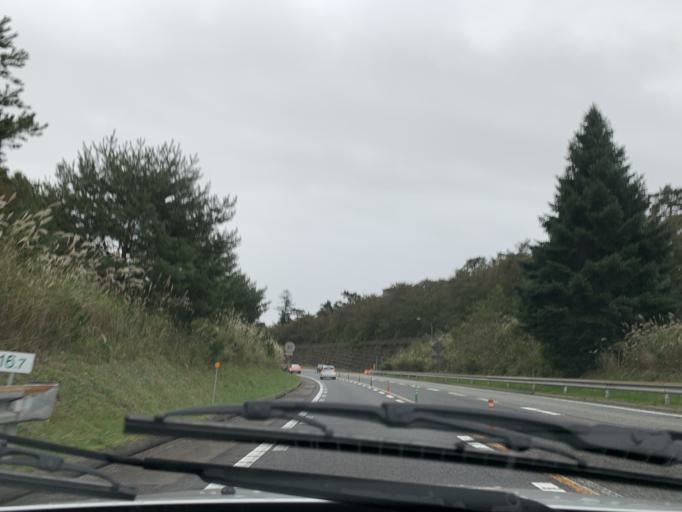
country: JP
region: Shizuoka
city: Gotemba
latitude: 35.3628
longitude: 138.8507
